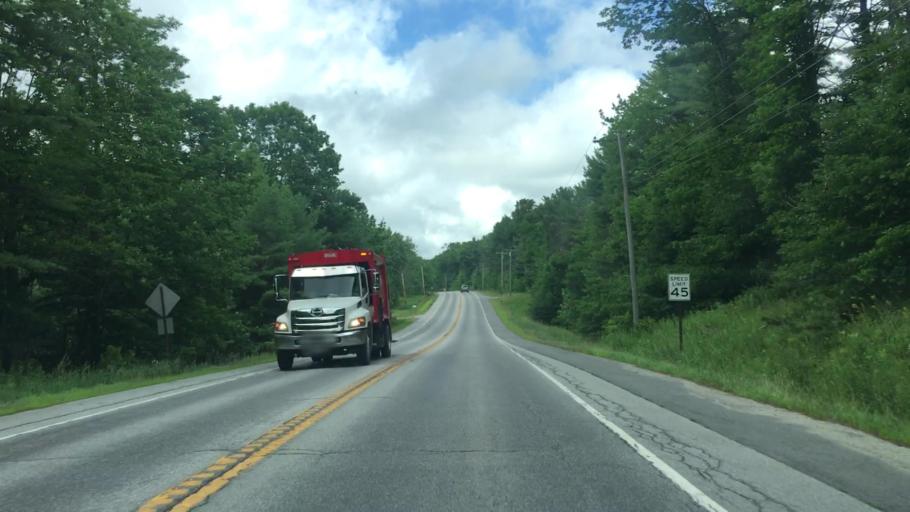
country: US
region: Maine
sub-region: Kennebec County
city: Farmingdale
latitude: 44.2614
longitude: -69.7646
